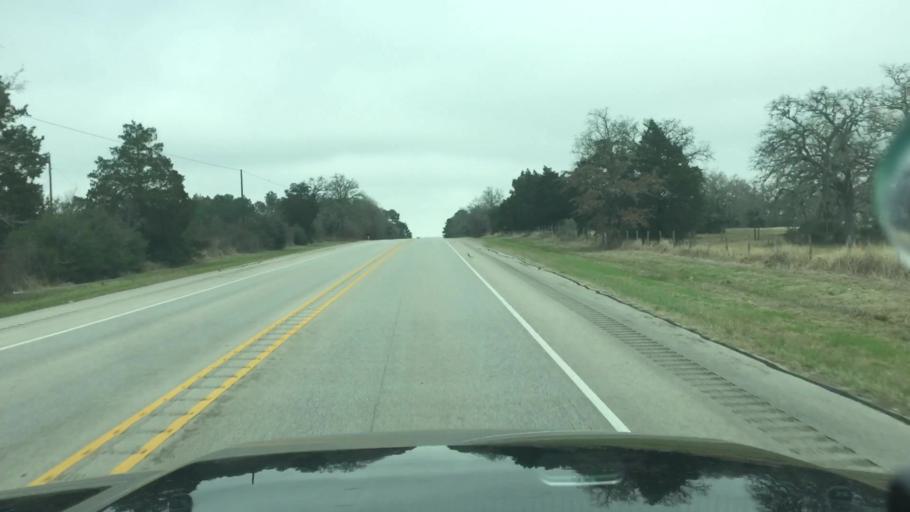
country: US
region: Texas
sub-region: Lee County
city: Giddings
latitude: 30.0755
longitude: -96.9170
